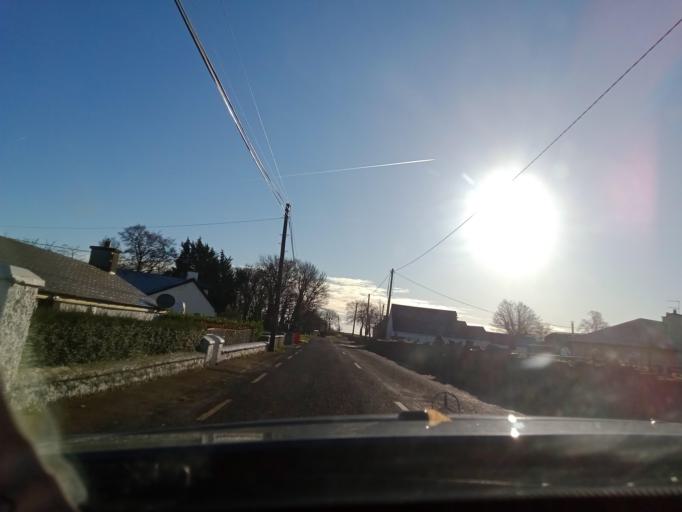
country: IE
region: Leinster
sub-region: Kilkenny
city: Piltown
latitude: 52.3718
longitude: -7.3364
